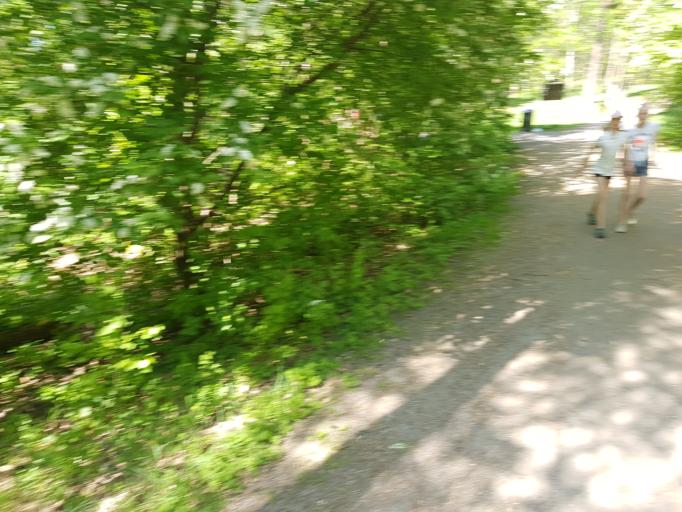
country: SE
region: Stockholm
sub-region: Stockholms Kommun
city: OEstermalm
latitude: 59.2972
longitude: 18.1082
